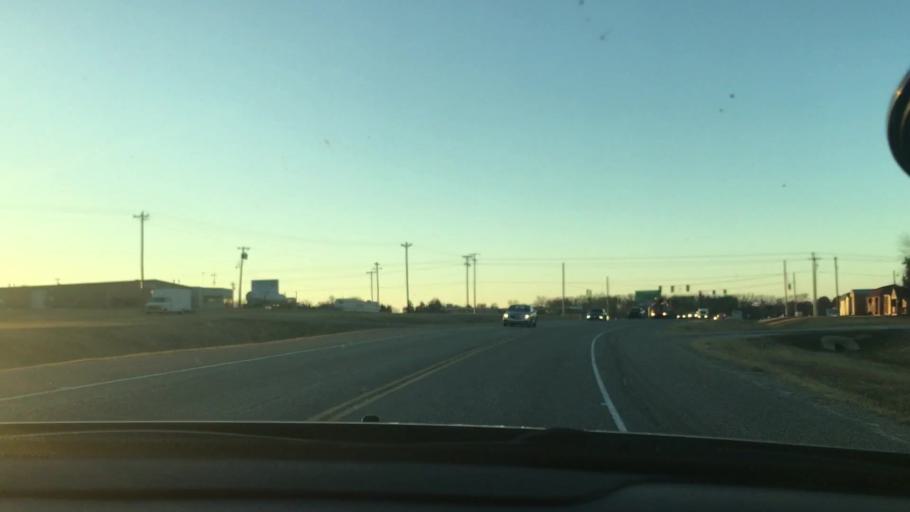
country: US
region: Oklahoma
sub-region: Pontotoc County
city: Ada
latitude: 34.7547
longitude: -96.7017
